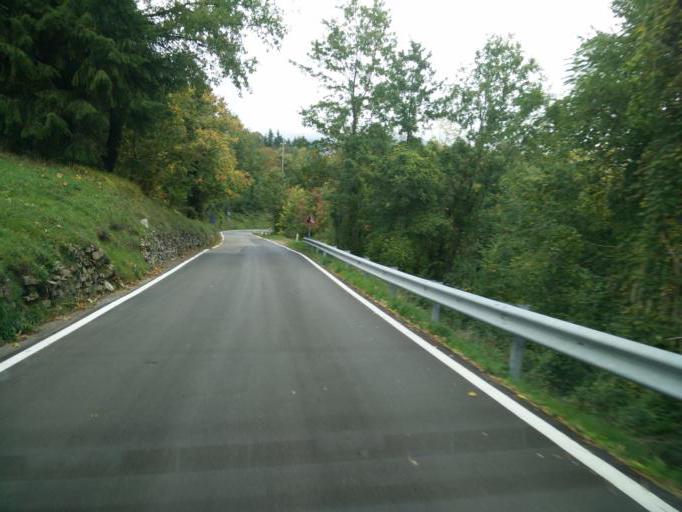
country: IT
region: Tuscany
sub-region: Provincia di Lucca
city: Giuncugnano
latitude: 44.2043
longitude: 10.2420
